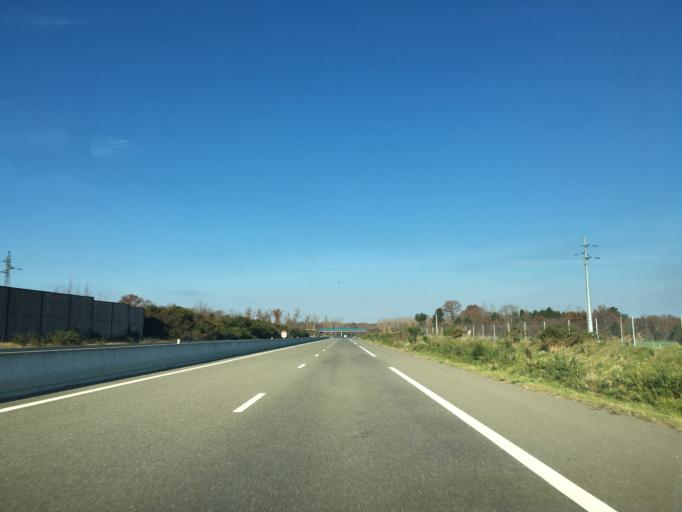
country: FR
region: Aquitaine
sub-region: Departement des Landes
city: Villeneuve-de-Marsan
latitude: 43.8637
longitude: -0.3568
